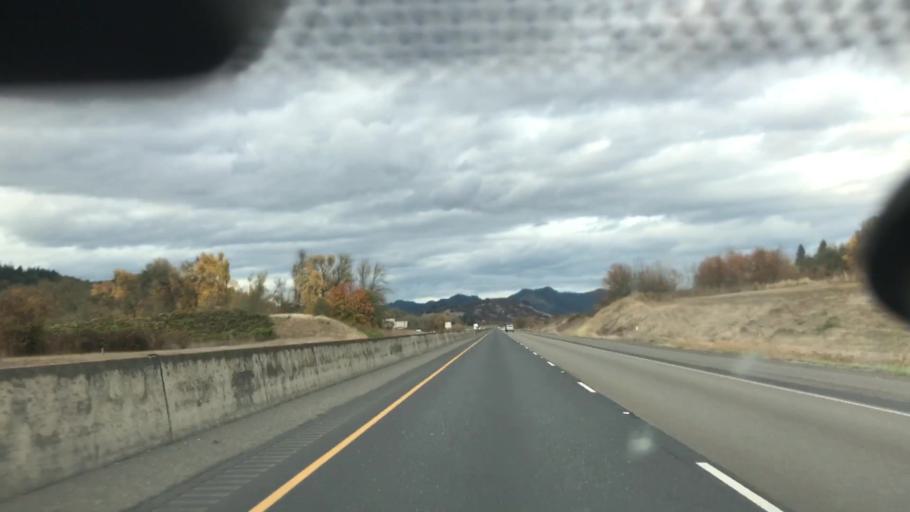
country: US
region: Oregon
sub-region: Douglas County
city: Yoncalla
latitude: 43.5493
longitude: -123.2866
